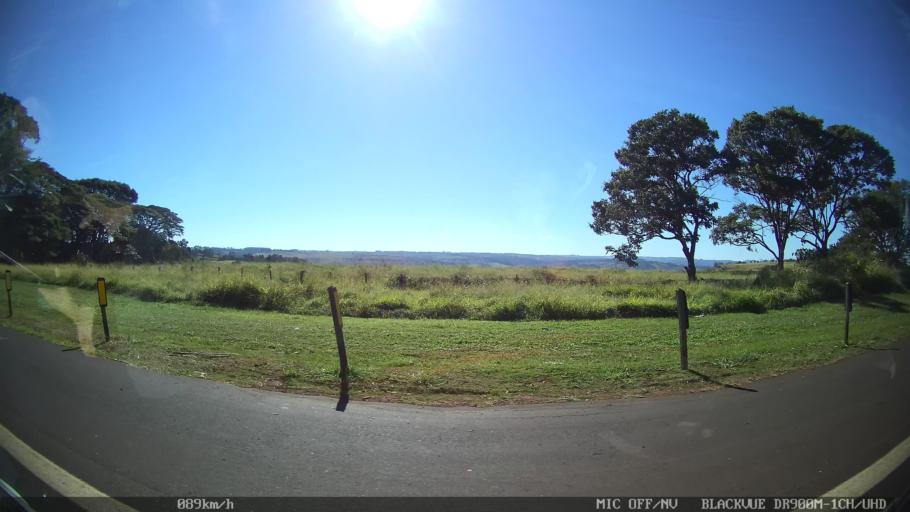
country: BR
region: Sao Paulo
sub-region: Franca
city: Franca
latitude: -20.5827
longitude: -47.3370
